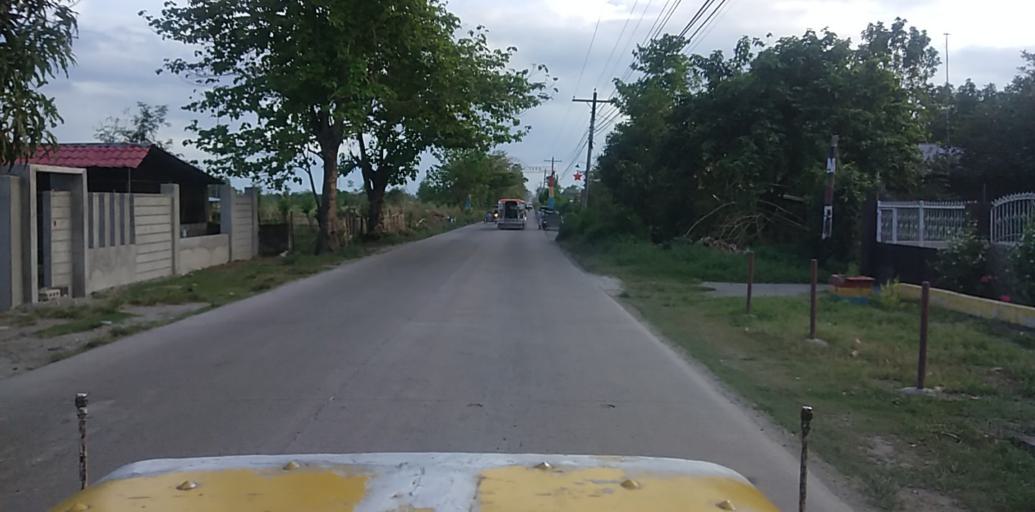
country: PH
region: Central Luzon
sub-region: Province of Pampanga
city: San Antonio
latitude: 15.1509
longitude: 120.6892
